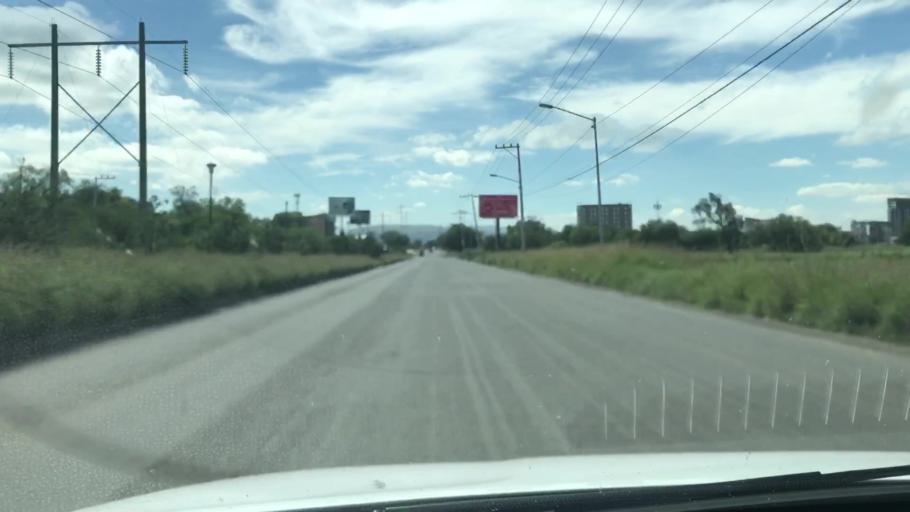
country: MX
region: Guanajuato
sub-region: Celaya
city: La Trinidad
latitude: 20.5391
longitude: -100.7788
